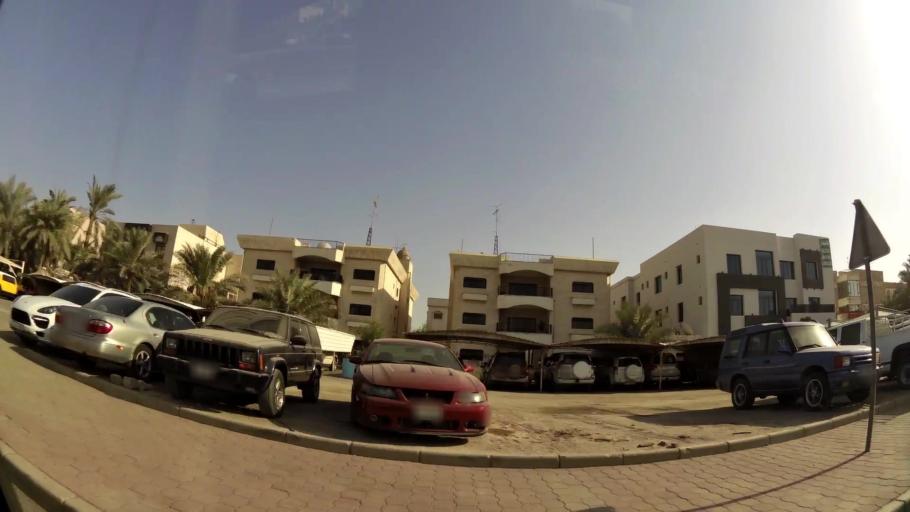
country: KW
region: Muhafazat Hawalli
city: Ar Rumaythiyah
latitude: 29.3064
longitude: 48.0652
